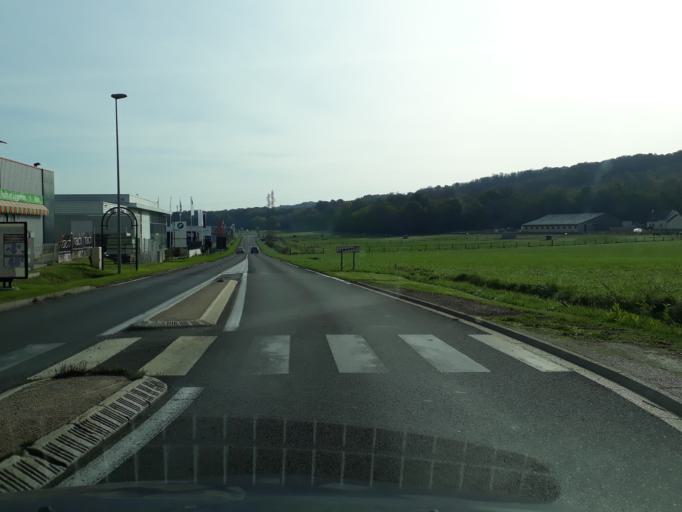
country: FR
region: Ile-de-France
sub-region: Departement de Seine-et-Marne
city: Vulaines-sur-Seine
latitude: 48.4248
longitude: 2.7623
